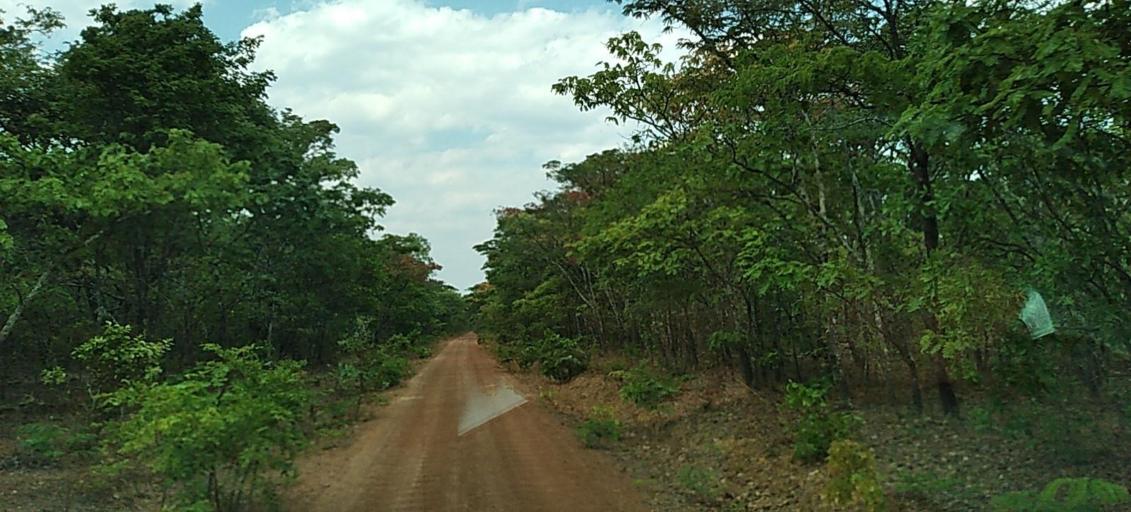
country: ZM
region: Copperbelt
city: Chililabombwe
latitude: -12.4594
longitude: 27.5982
